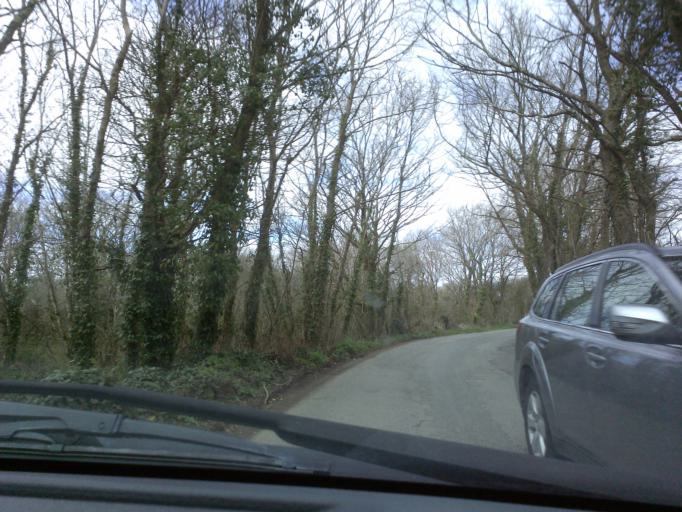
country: GB
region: England
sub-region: Cornwall
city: St. Buryan
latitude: 50.0580
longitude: -5.6243
